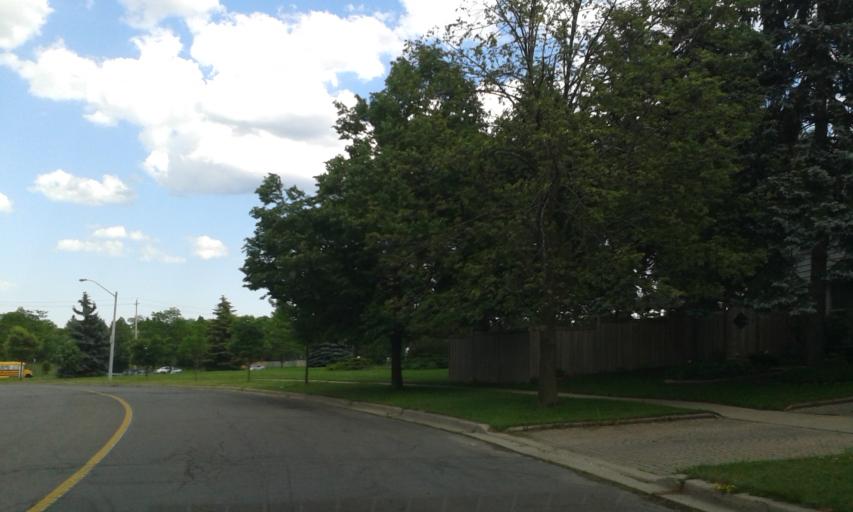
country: CA
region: Ontario
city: Scarborough
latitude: 43.8050
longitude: -79.2675
